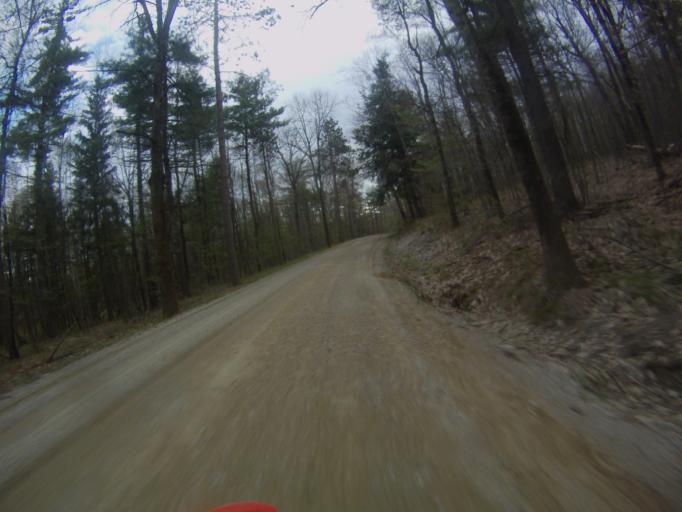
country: US
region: Vermont
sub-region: Addison County
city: Middlebury (village)
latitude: 43.9739
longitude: -73.0786
